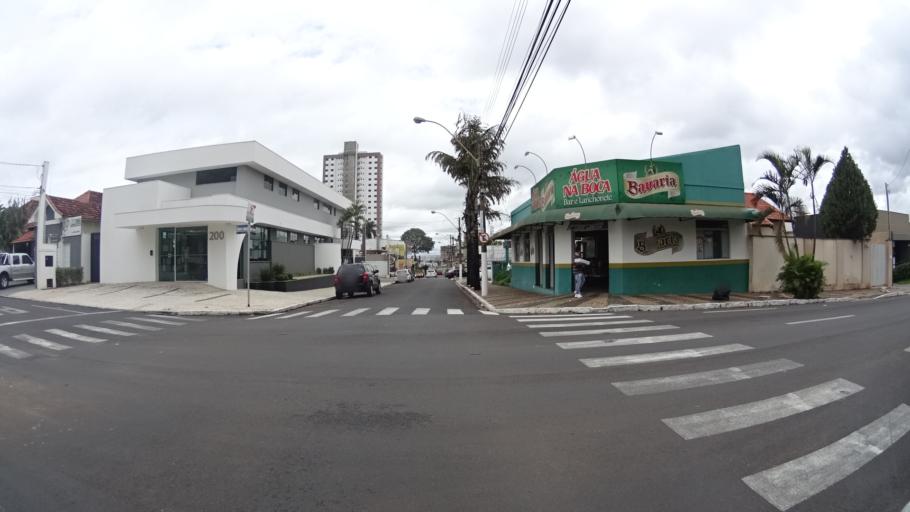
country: BR
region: Sao Paulo
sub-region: Marilia
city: Marilia
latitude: -22.2210
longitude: -49.9468
